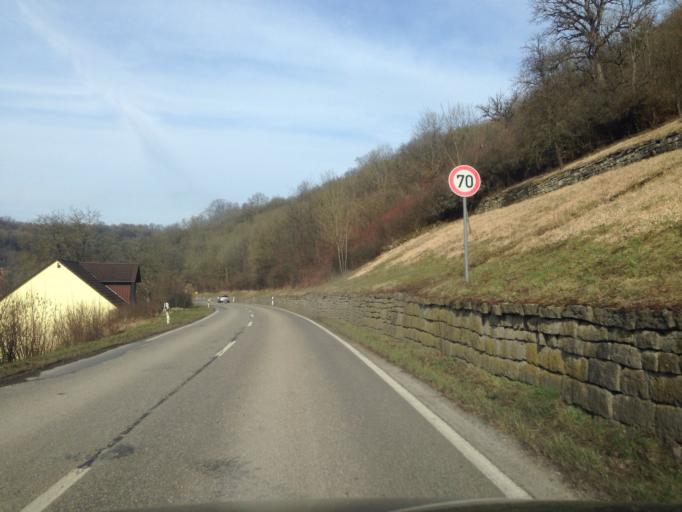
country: DE
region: Baden-Wuerttemberg
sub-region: Regierungsbezirk Stuttgart
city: Widdern
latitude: 49.3168
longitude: 9.4278
